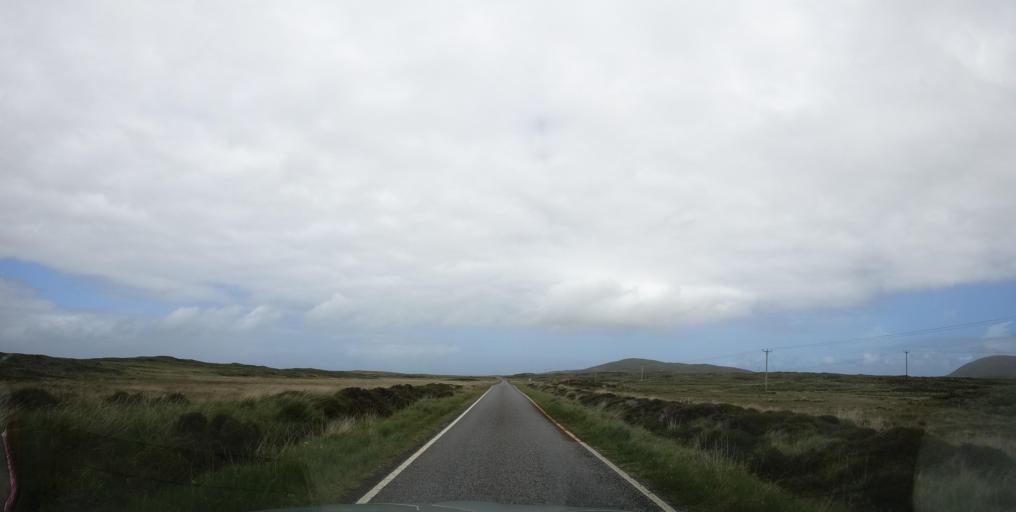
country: GB
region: Scotland
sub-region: Eilean Siar
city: Isle of South Uist
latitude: 57.2769
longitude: -7.3660
